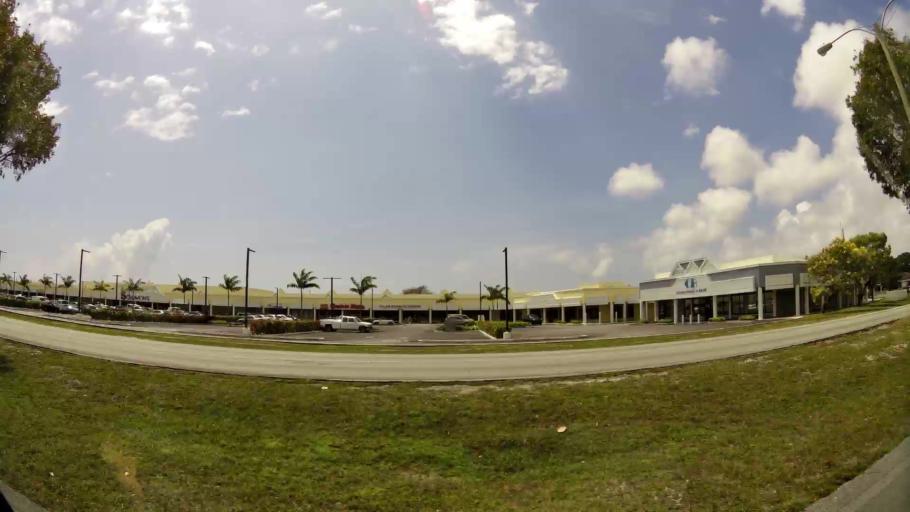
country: BS
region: Freeport
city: Lucaya
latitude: 26.5213
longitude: -78.6567
